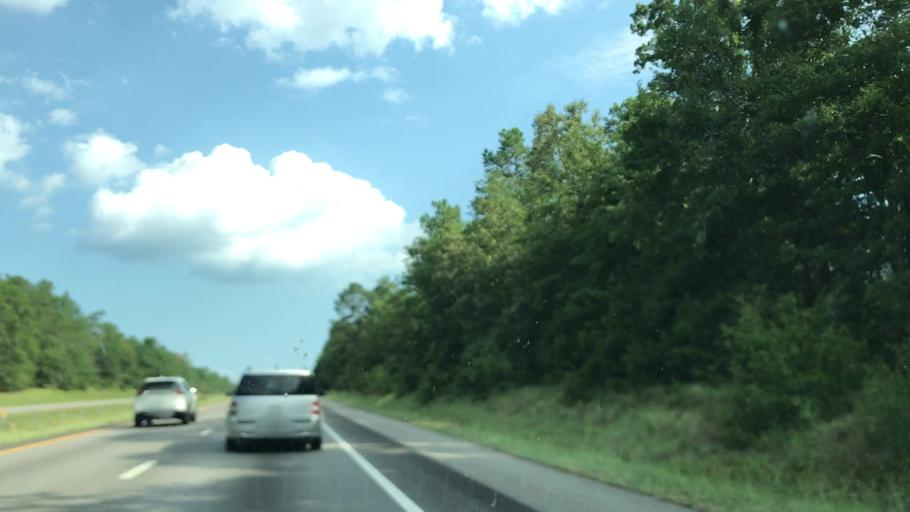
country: US
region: South Carolina
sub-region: Calhoun County
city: Oak Grove
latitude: 33.7203
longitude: -80.9259
